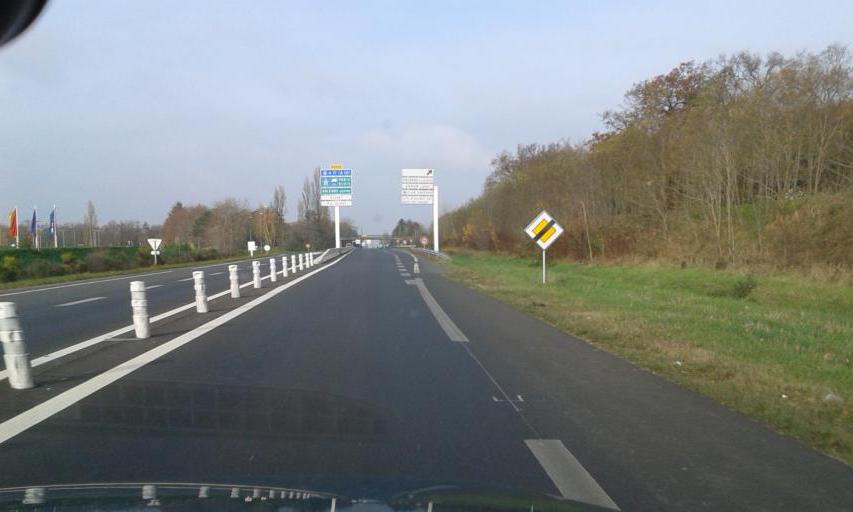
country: FR
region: Centre
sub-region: Departement du Loiret
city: Olivet
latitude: 47.8271
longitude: 1.9212
